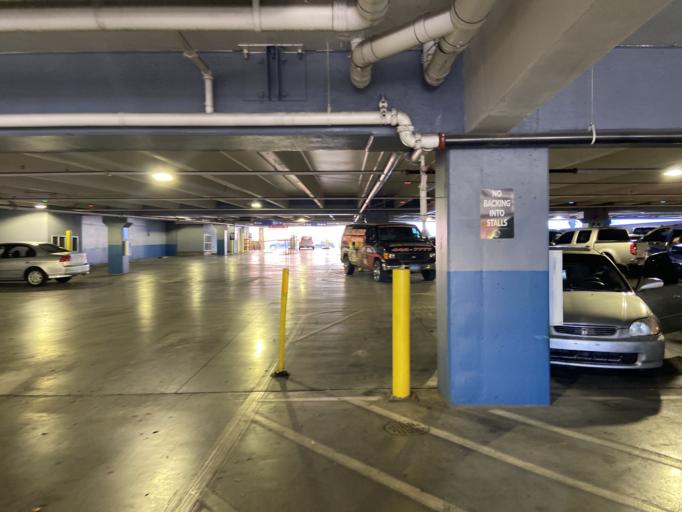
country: US
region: Nevada
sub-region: Clark County
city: Las Vegas
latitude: 36.1657
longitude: -115.1449
